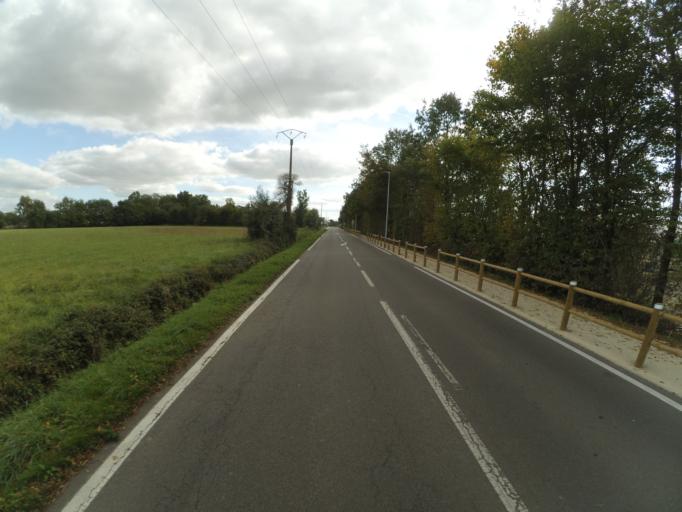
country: FR
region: Pays de la Loire
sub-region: Departement de la Loire-Atlantique
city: Carquefou
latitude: 47.3077
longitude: -1.5055
